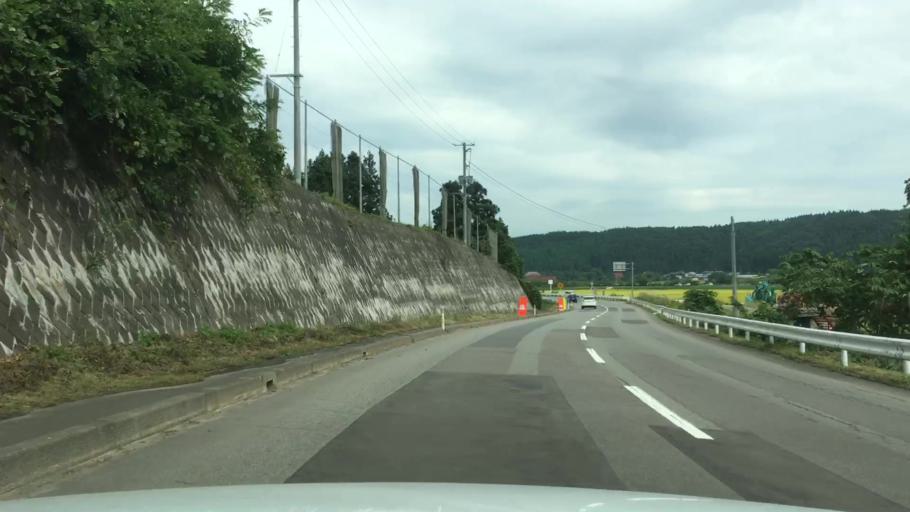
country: JP
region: Aomori
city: Shimokizukuri
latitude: 40.7520
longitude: 140.2295
